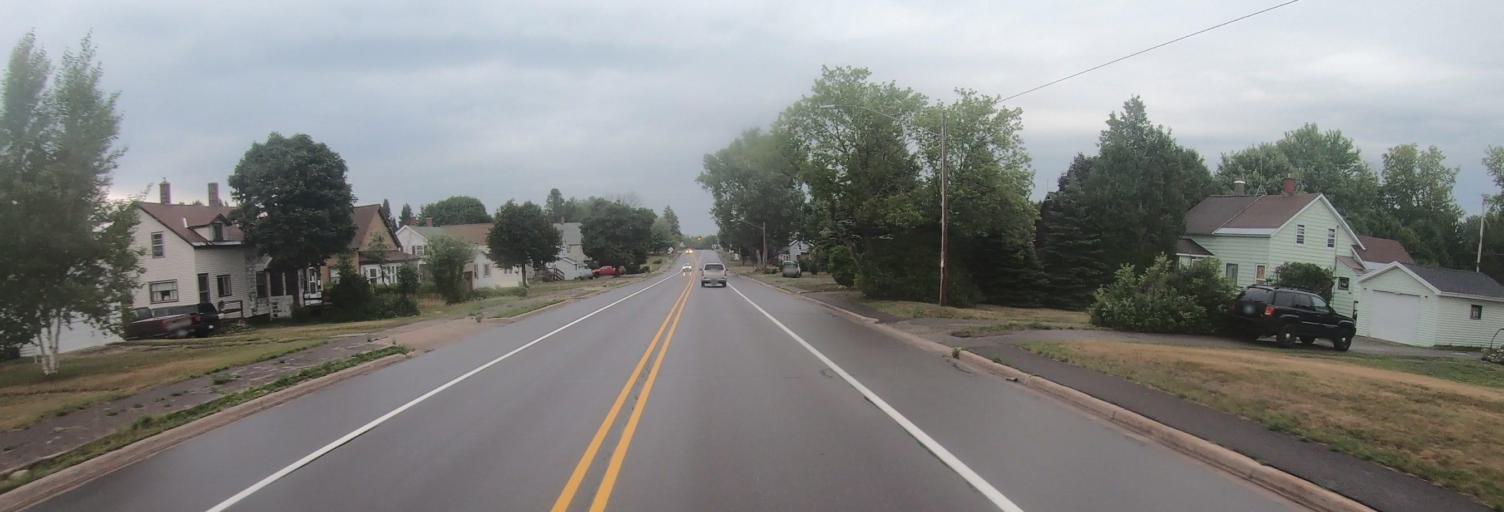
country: US
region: Michigan
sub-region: Houghton County
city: Laurium
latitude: 47.2476
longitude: -88.4420
